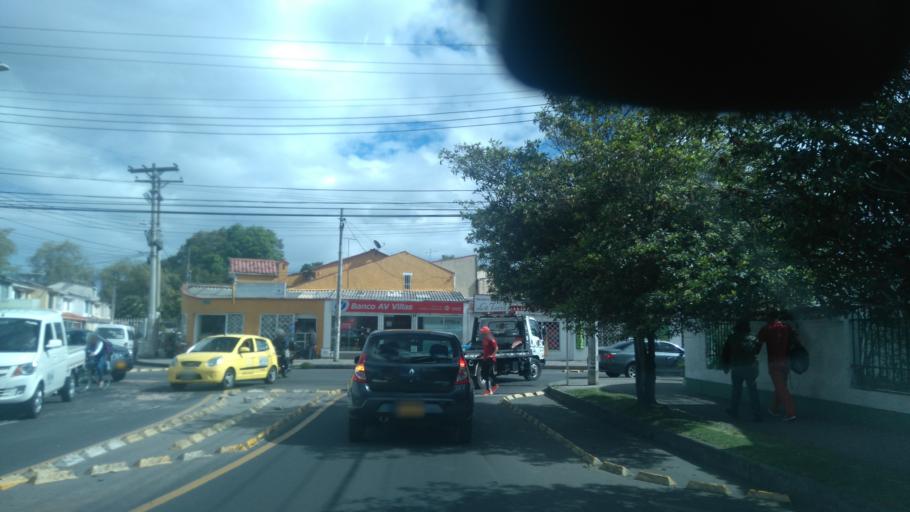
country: CO
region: Cundinamarca
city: Cota
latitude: 4.7564
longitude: -74.0515
